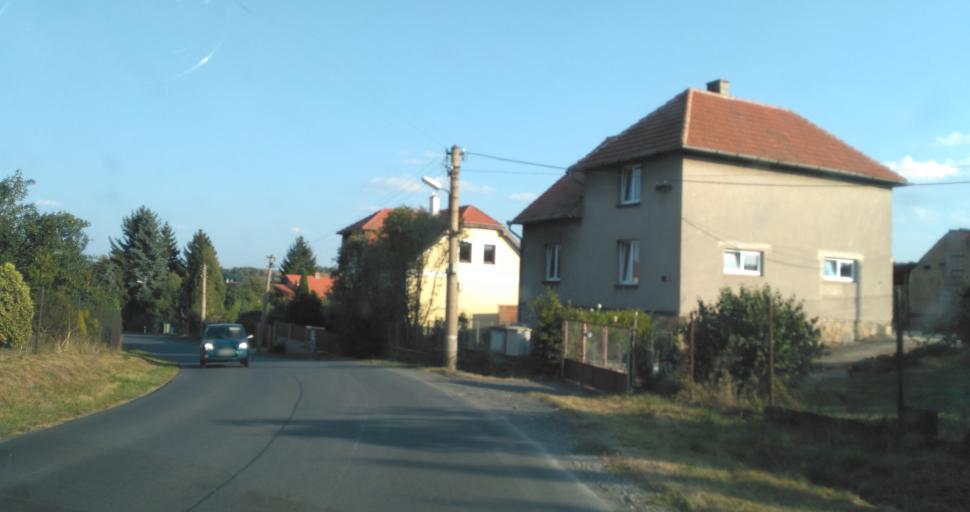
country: CZ
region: Central Bohemia
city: Hudlice
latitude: 49.9592
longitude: 13.9778
